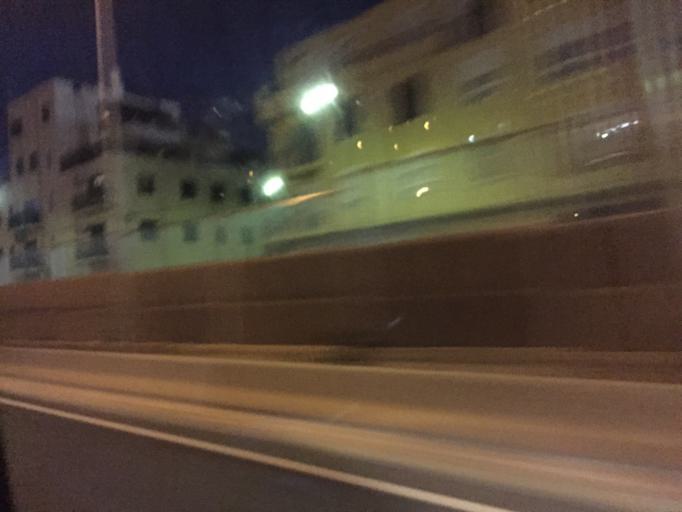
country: ES
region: Balearic Islands
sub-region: Illes Balears
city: Palma
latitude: 39.5810
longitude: 2.6737
